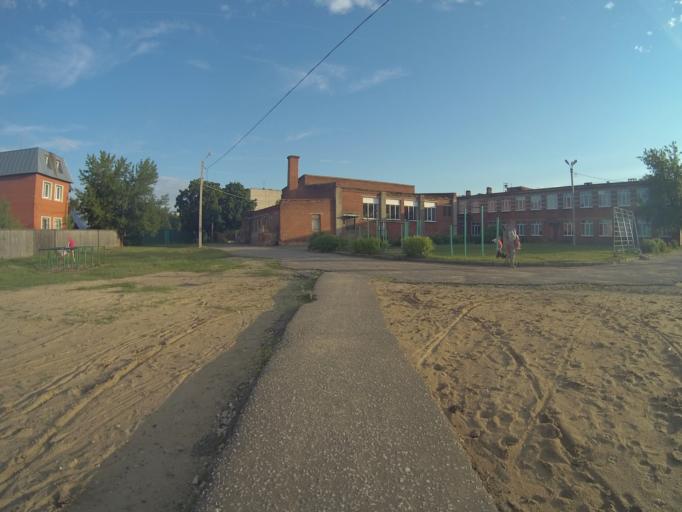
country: RU
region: Vladimir
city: Kommunar
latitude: 56.1092
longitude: 40.4436
